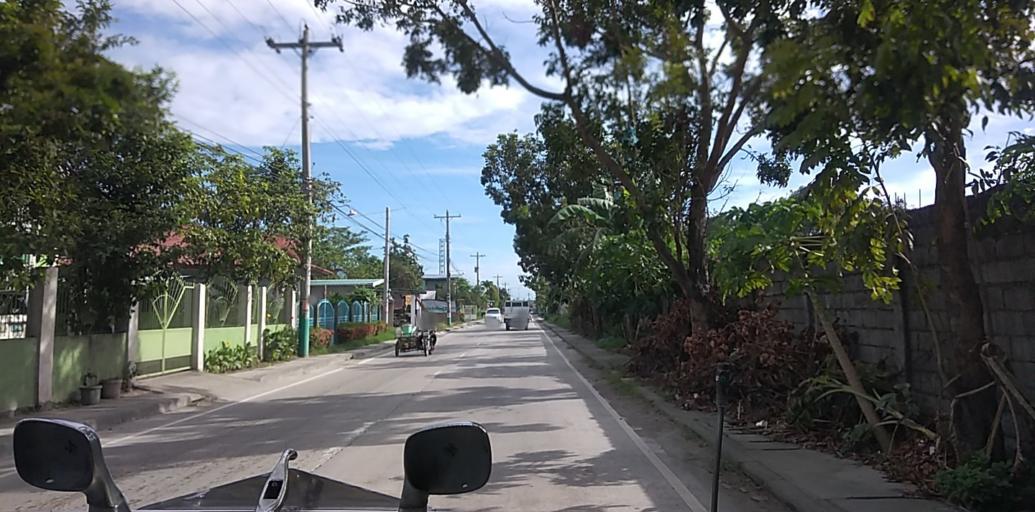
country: PH
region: Central Luzon
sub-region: Province of Pampanga
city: Malino
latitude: 15.1249
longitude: 120.6692
